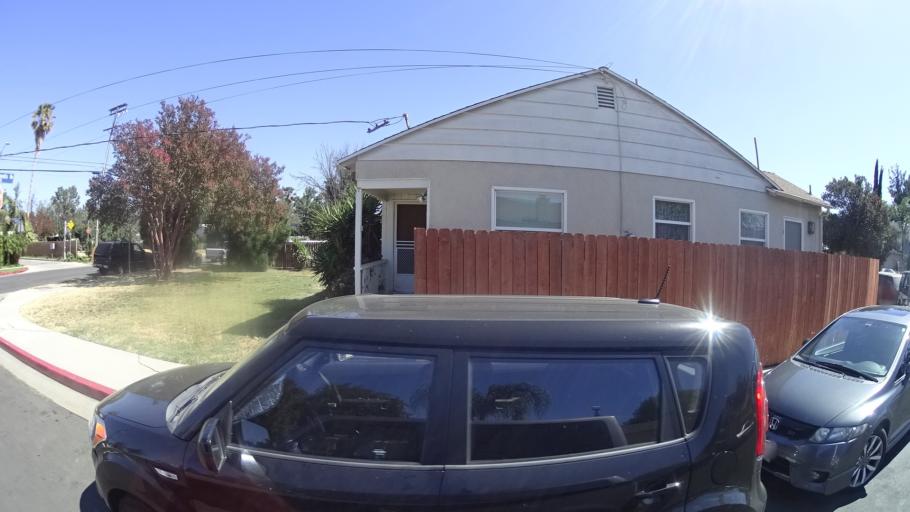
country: US
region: California
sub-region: Los Angeles County
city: Van Nuys
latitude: 34.1925
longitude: -118.4818
